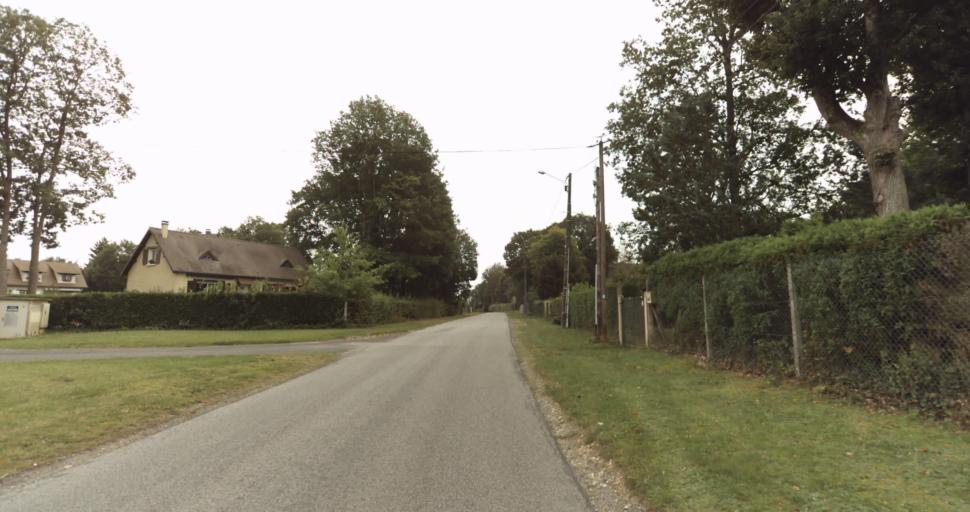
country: FR
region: Haute-Normandie
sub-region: Departement de l'Eure
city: Croth
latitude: 48.8695
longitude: 1.3570
